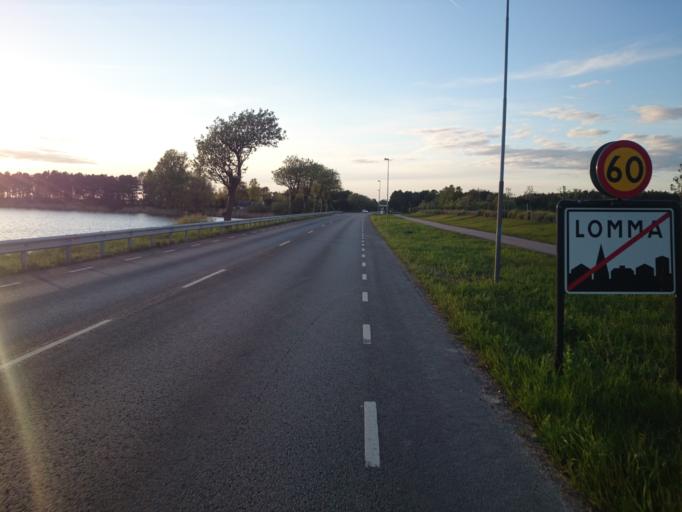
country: SE
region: Skane
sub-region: Lomma Kommun
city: Lomma
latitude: 55.6844
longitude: 13.0650
